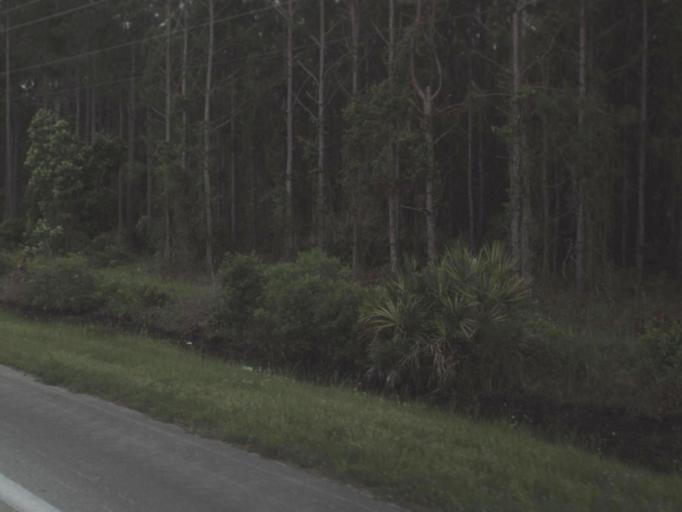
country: US
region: Florida
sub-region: Saint Johns County
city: Saint Augustine Shores
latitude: 29.7531
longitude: -81.3342
